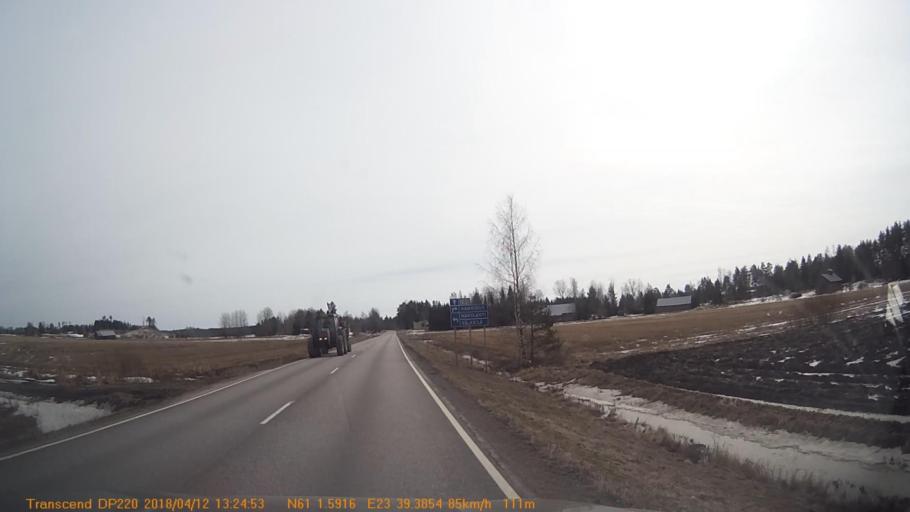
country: FI
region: Pirkanmaa
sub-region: Etelae-Pirkanmaa
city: Kylmaekoski
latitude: 61.0254
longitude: 23.6574
